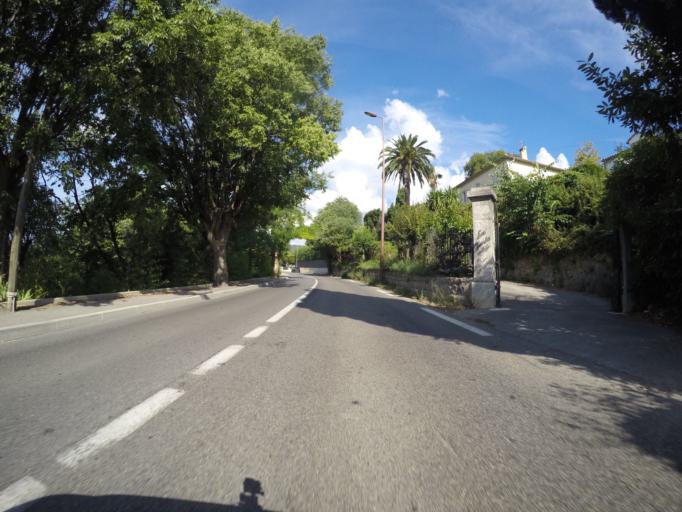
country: FR
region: Provence-Alpes-Cote d'Azur
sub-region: Departement des Alpes-Maritimes
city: Opio
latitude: 43.6749
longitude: 6.9877
